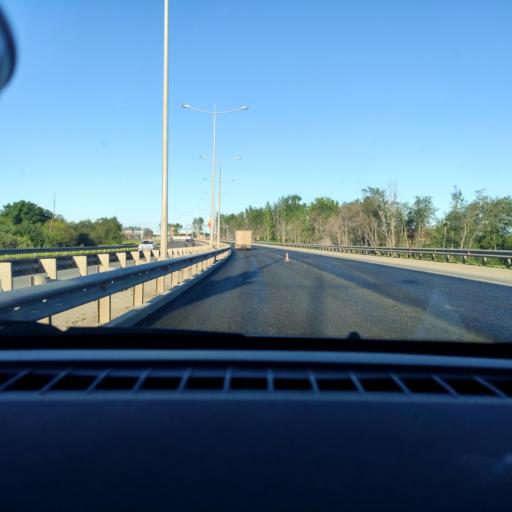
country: RU
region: Perm
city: Kondratovo
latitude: 57.9357
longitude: 56.0301
